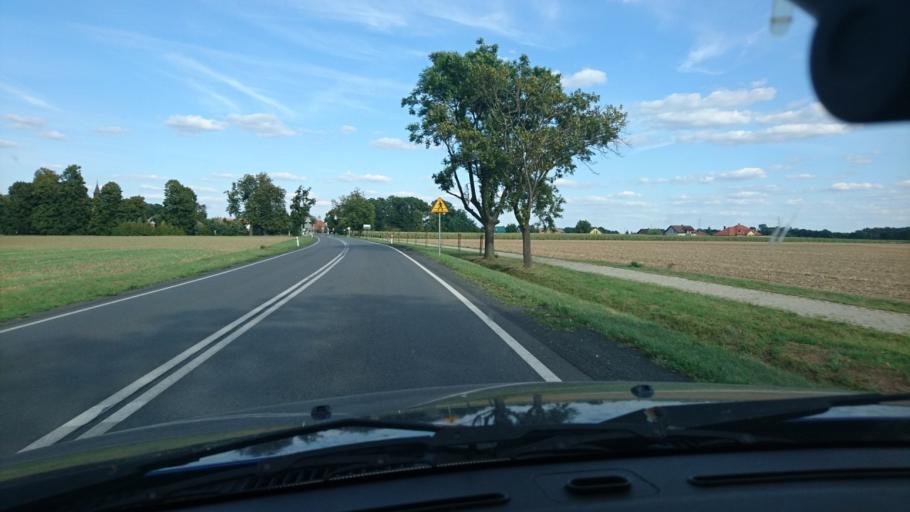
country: PL
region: Greater Poland Voivodeship
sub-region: Powiat krotoszynski
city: Krotoszyn
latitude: 51.7174
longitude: 17.3703
